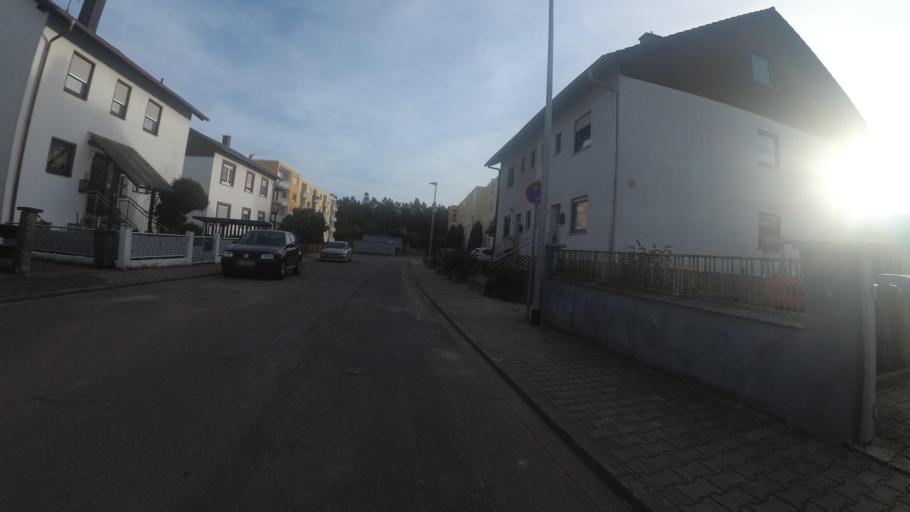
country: DE
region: Rheinland-Pfalz
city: Ramstein-Miesenbach
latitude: 49.4392
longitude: 7.5495
